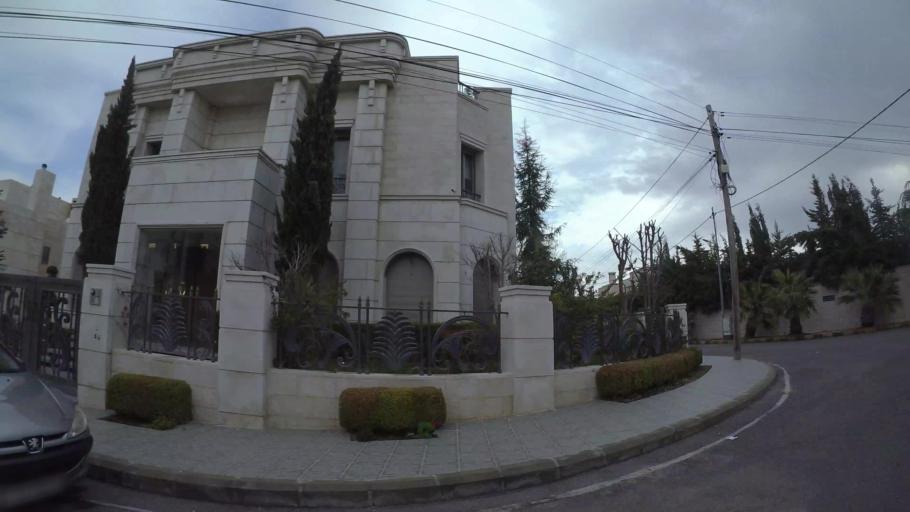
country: JO
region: Amman
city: Wadi as Sir
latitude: 31.9885
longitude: 35.8201
